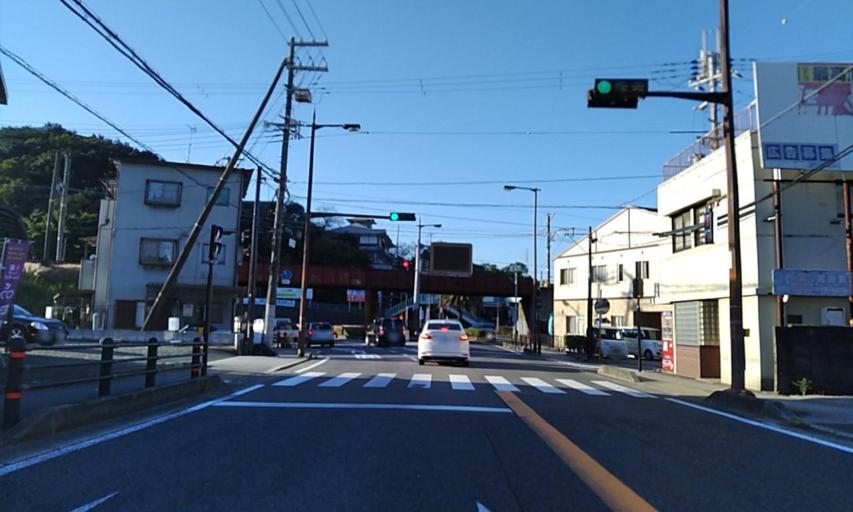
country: JP
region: Wakayama
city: Wakayama-shi
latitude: 34.3189
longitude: 135.1494
